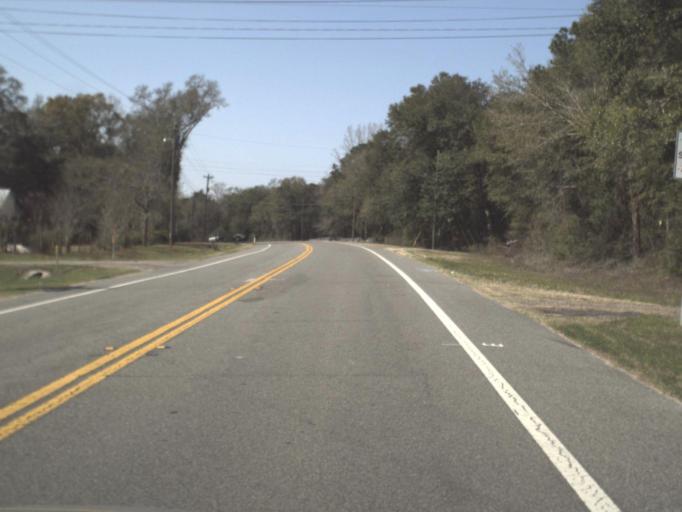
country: US
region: Florida
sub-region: Gadsden County
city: Havana
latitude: 30.6077
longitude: -84.4727
